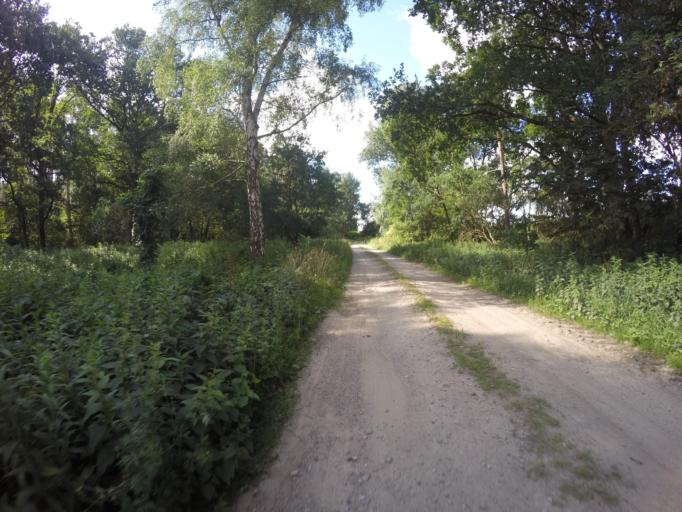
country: DE
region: Lower Saxony
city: Neetze
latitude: 53.2650
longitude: 10.6529
